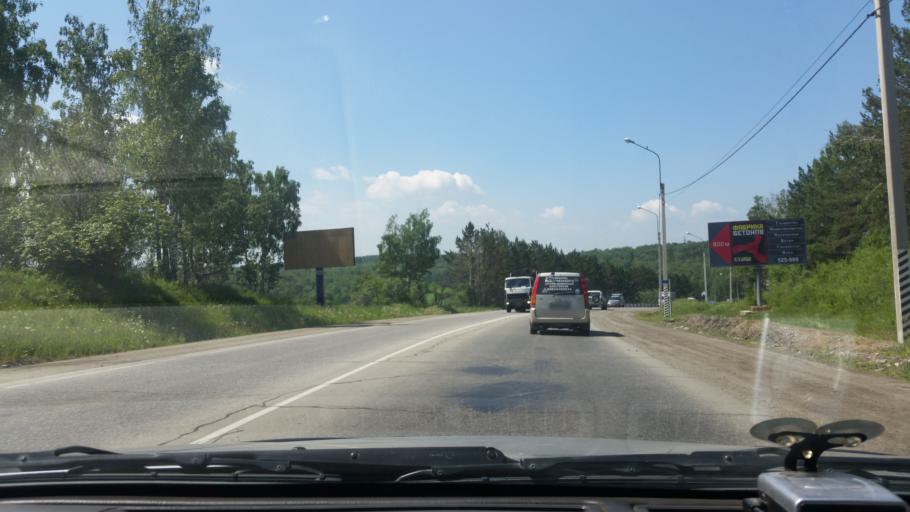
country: RU
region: Irkutsk
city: Smolenshchina
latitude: 52.2535
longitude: 104.1743
